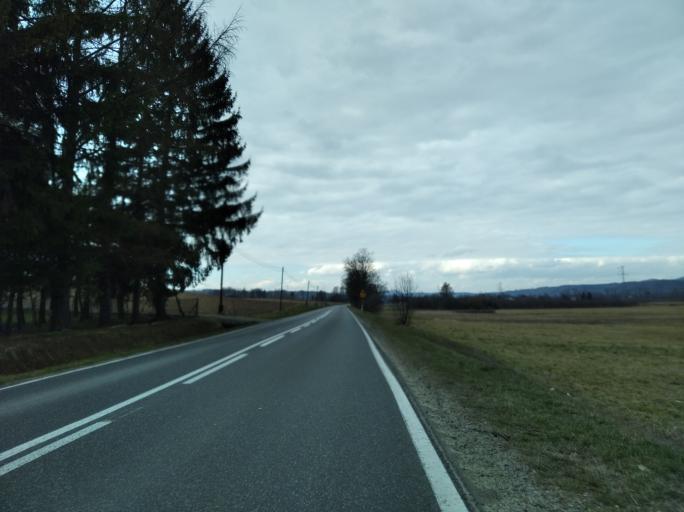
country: PL
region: Subcarpathian Voivodeship
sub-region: Powiat krosnienski
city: Wojaszowka
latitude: 49.7852
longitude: 21.6632
